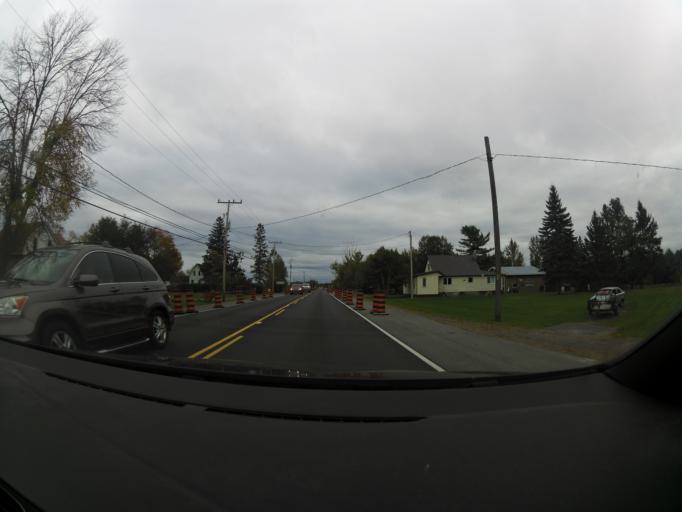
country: CA
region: Ontario
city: Bells Corners
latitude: 45.4201
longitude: -76.0176
